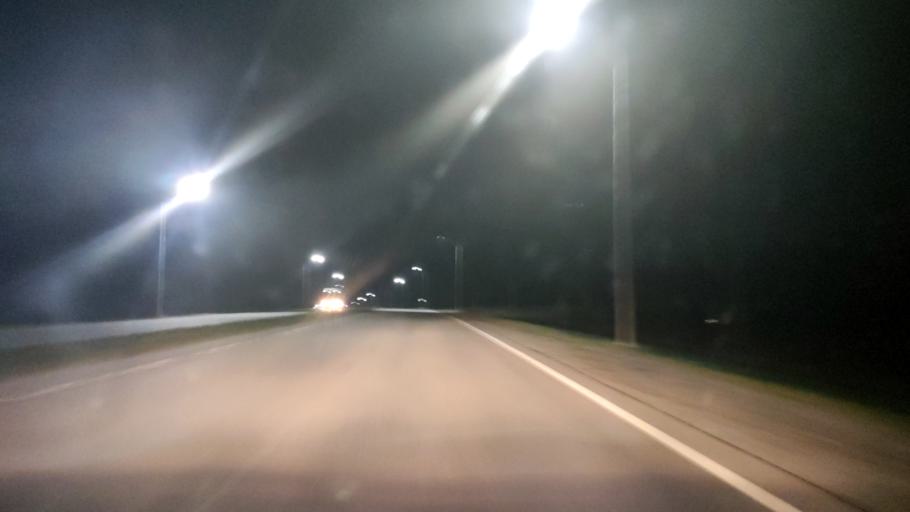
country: RU
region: Belgorod
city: Staryy Oskol
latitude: 51.3940
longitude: 37.8700
